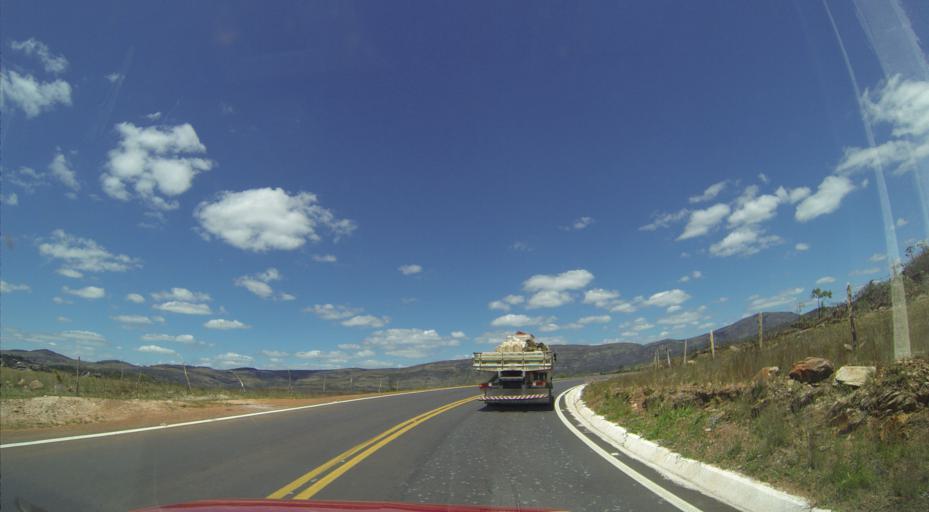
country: BR
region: Minas Gerais
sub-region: Conceicao Do Mato Dentro
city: Conceicao do Mato Dentro
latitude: -19.2854
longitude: -43.5748
